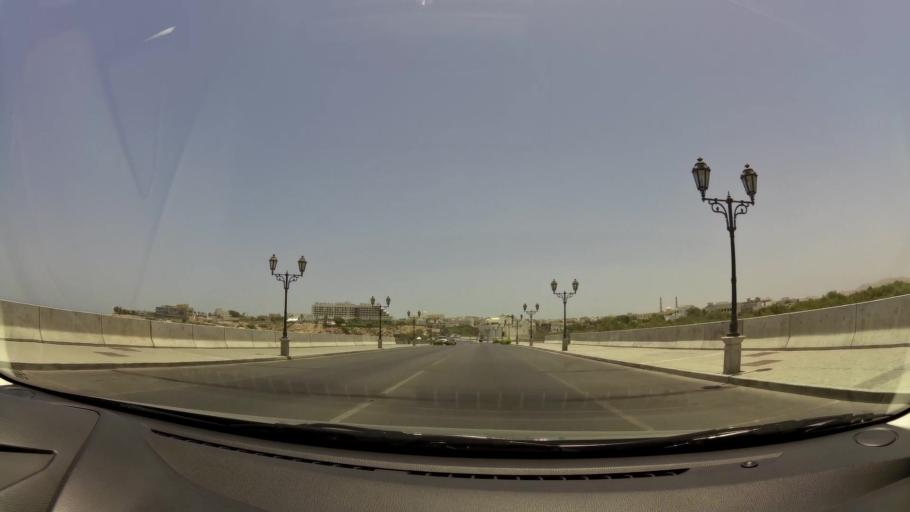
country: OM
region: Muhafazat Masqat
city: Bawshar
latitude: 23.6246
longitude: 58.4791
